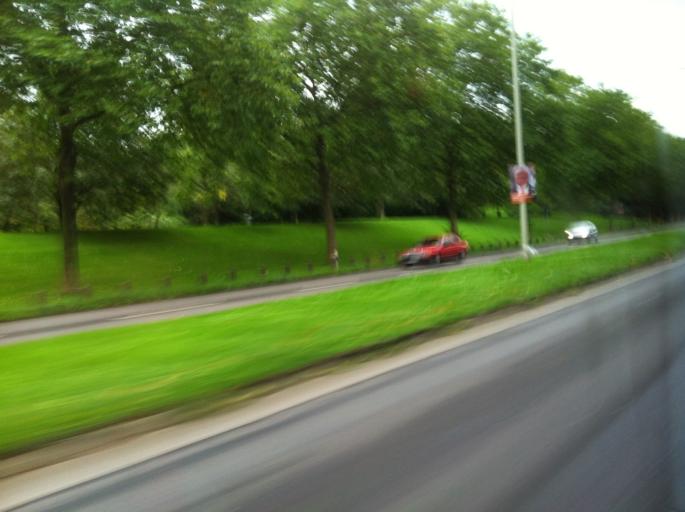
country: DE
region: North Rhine-Westphalia
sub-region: Regierungsbezirk Koln
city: Bonn
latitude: 50.7130
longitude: 7.1347
